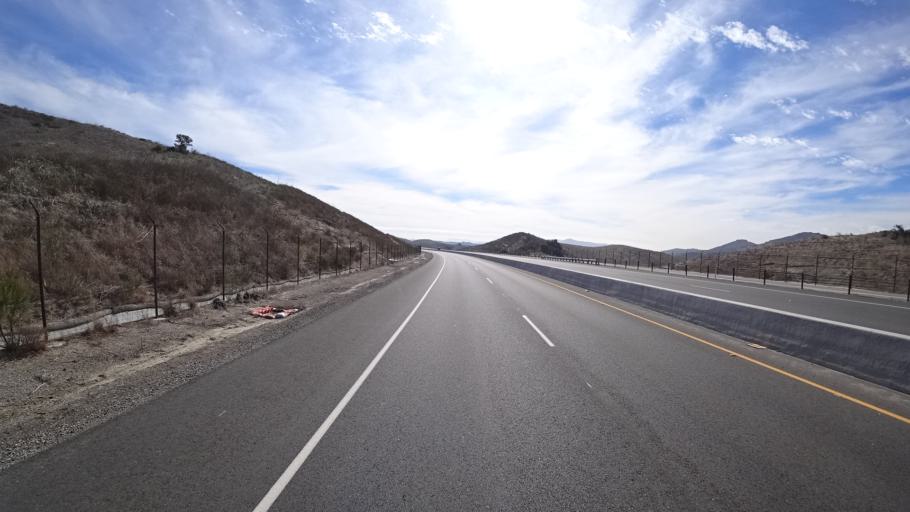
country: US
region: California
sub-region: Orange County
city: Ladera Ranch
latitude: 33.5656
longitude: -117.6120
